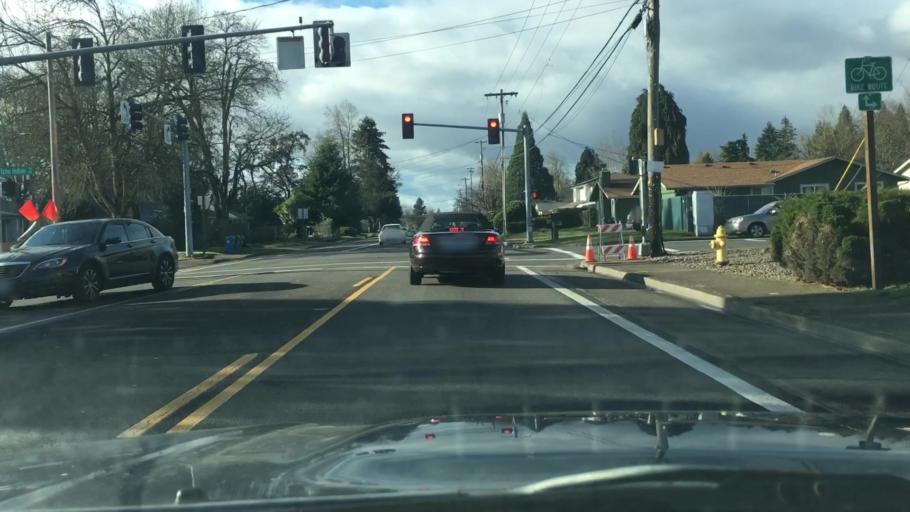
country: US
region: Oregon
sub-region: Lane County
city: Eugene
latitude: 44.0700
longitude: -123.1677
